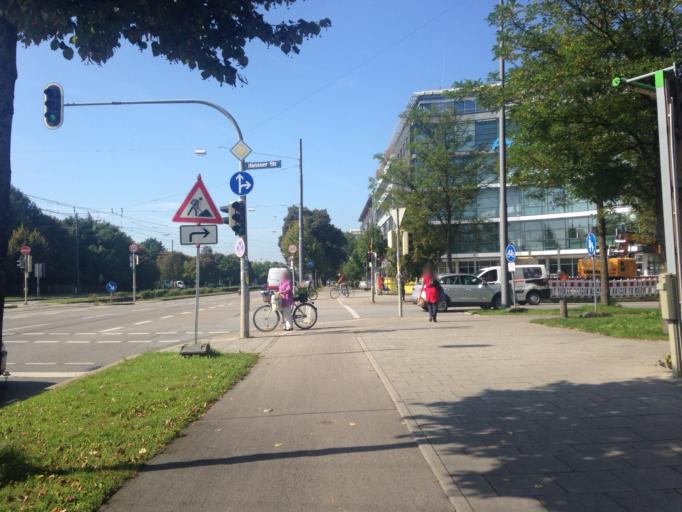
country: DE
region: Bavaria
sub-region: Upper Bavaria
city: Munich
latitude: 48.1725
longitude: 11.5287
